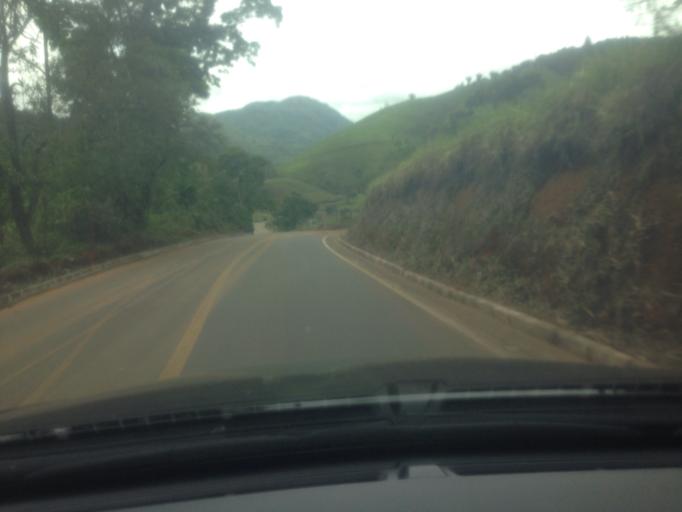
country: BR
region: Espirito Santo
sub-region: Guarapari
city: Guarapari
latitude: -20.5602
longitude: -40.5527
